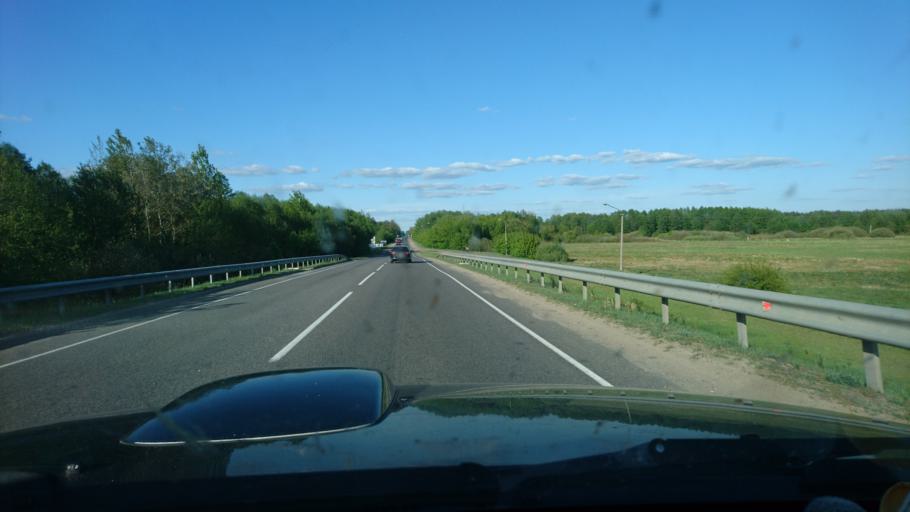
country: BY
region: Brest
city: Byaroza
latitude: 52.5422
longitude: 25.0005
